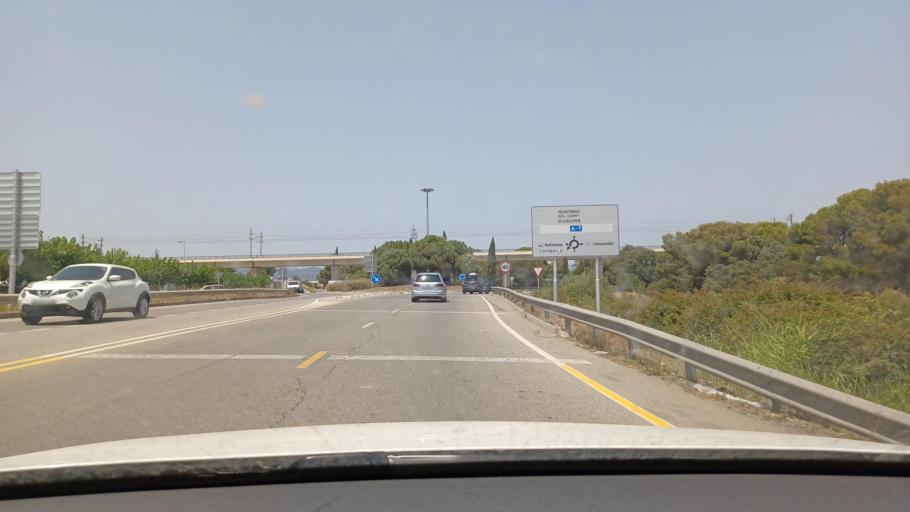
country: ES
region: Catalonia
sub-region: Provincia de Tarragona
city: Cambrils
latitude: 41.0778
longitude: 1.0405
